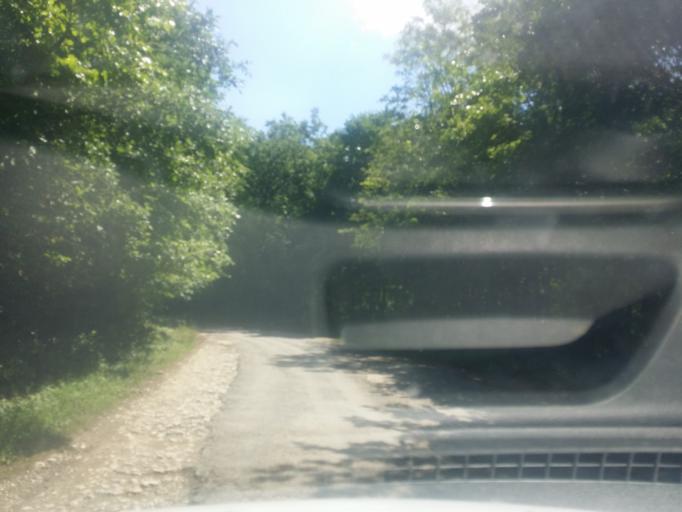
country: HU
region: Komarom-Esztergom
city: Piliscsev
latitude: 47.7050
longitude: 18.8288
